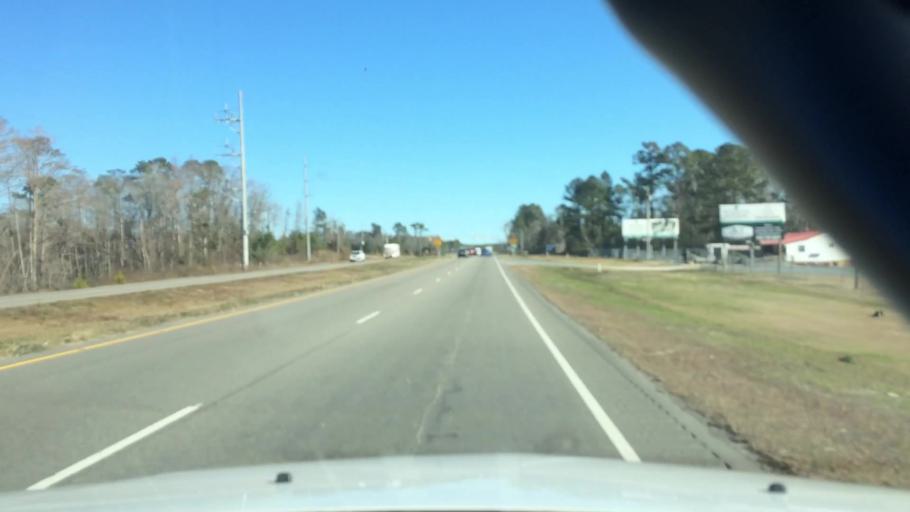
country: US
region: North Carolina
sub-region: Brunswick County
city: Bolivia
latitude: 34.0240
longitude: -78.2627
